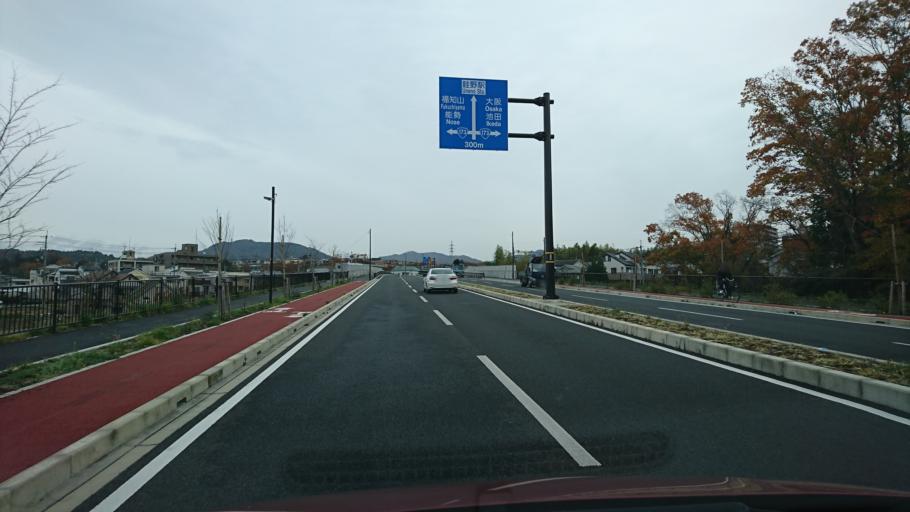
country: JP
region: Osaka
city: Ikeda
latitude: 34.8834
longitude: 135.4114
